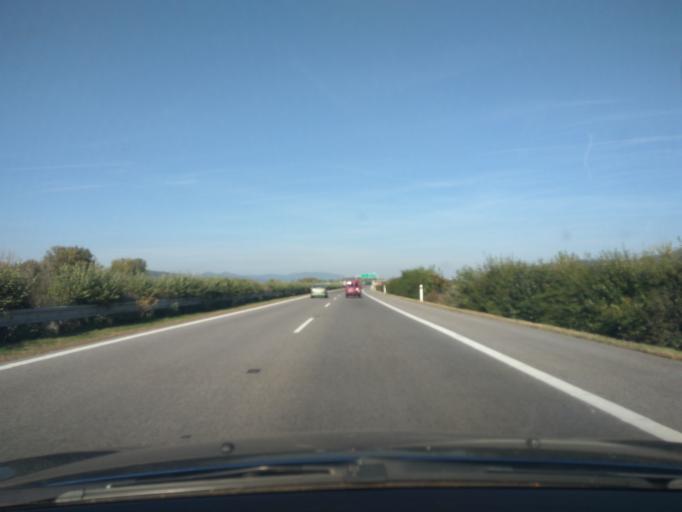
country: SK
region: Trenciansky
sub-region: Okres Nove Mesto nad Vahom
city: Nove Mesto nad Vahom
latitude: 48.7547
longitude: 17.8624
